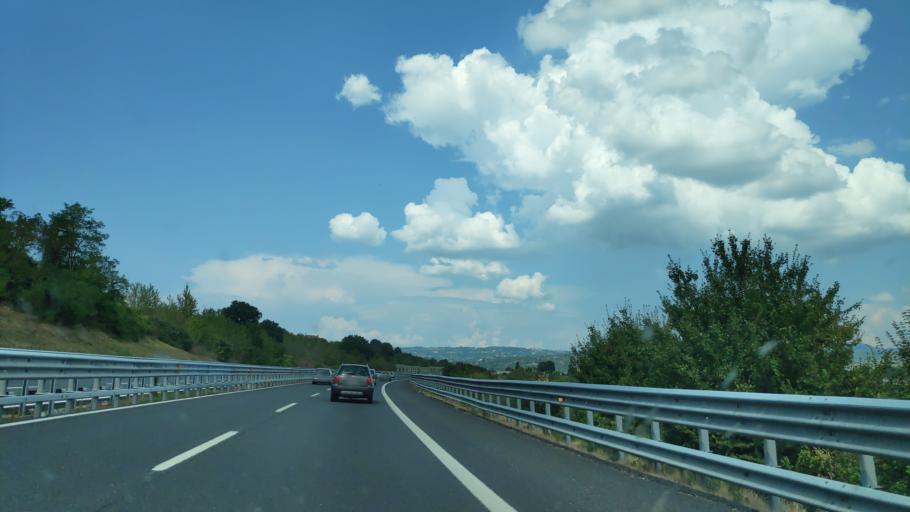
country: IT
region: Umbria
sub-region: Provincia di Terni
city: Fabro Scalo
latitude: 42.8512
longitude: 12.0376
